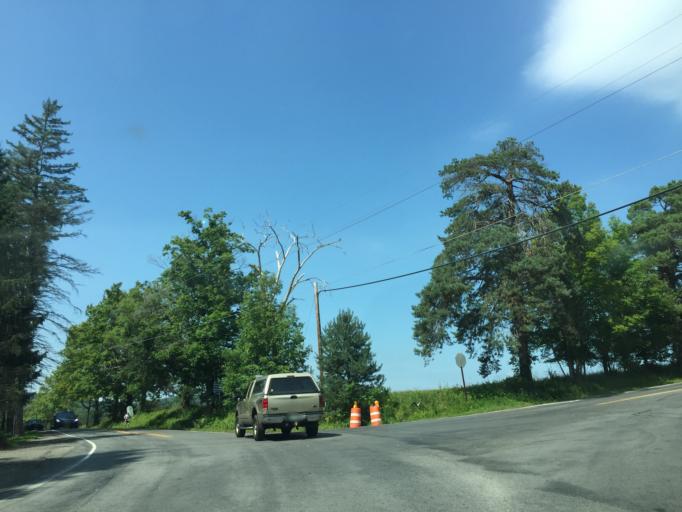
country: US
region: New York
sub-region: Otsego County
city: Cooperstown
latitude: 42.6864
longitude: -74.9179
